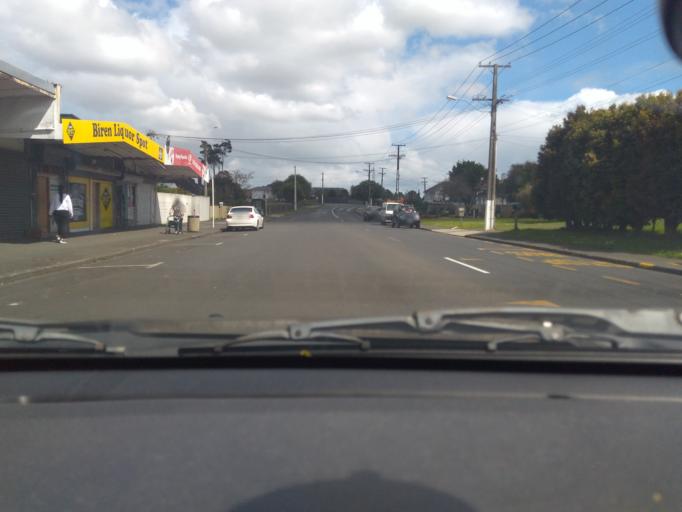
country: NZ
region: Auckland
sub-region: Auckland
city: Tamaki
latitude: -36.9256
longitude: 174.8568
